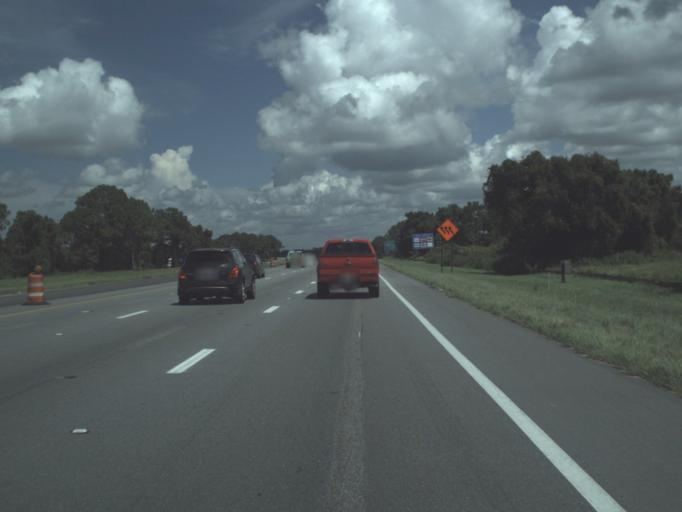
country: US
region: Florida
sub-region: Sarasota County
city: The Meadows
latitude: 27.3695
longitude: -82.4458
